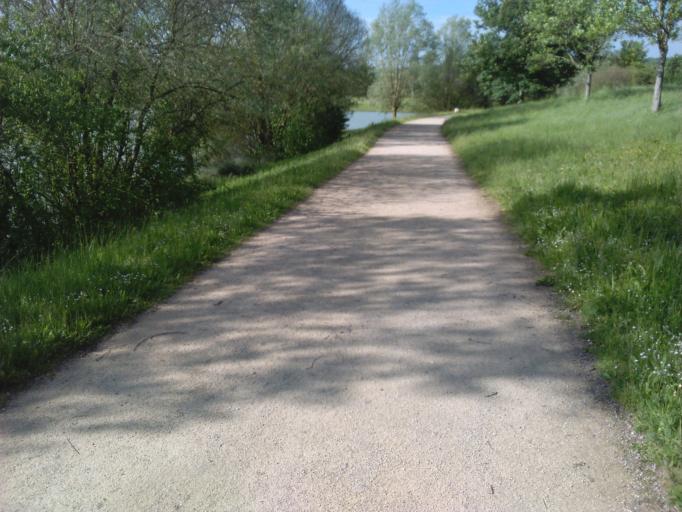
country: FR
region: Centre
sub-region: Departement du Loir-et-Cher
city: Villiers-sur-Loir
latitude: 47.7999
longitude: 0.9885
